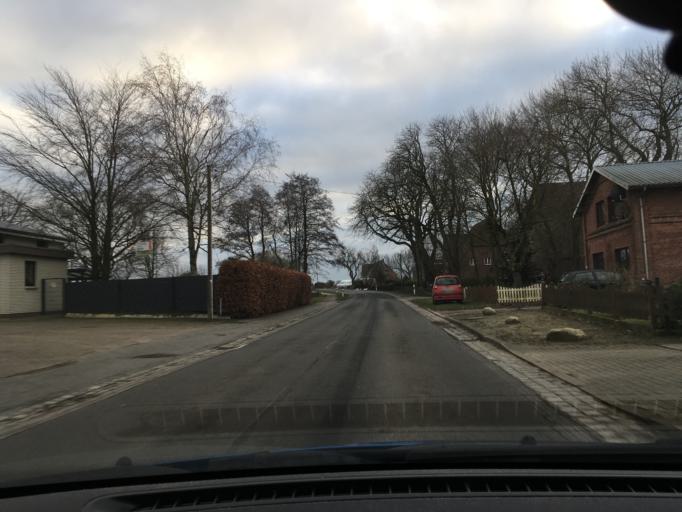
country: DE
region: Schleswig-Holstein
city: Lohe-Rickelshof
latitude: 54.1907
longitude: 9.0590
